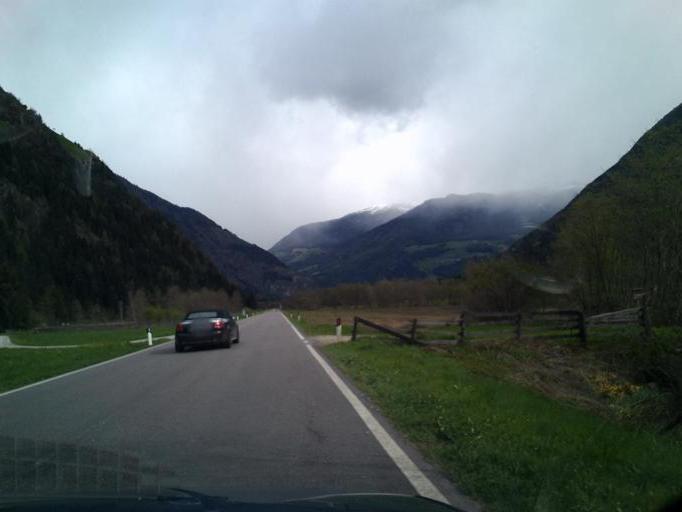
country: IT
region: Trentino-Alto Adige
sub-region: Bolzano
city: Molini di Tures
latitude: 46.8740
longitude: 11.9481
